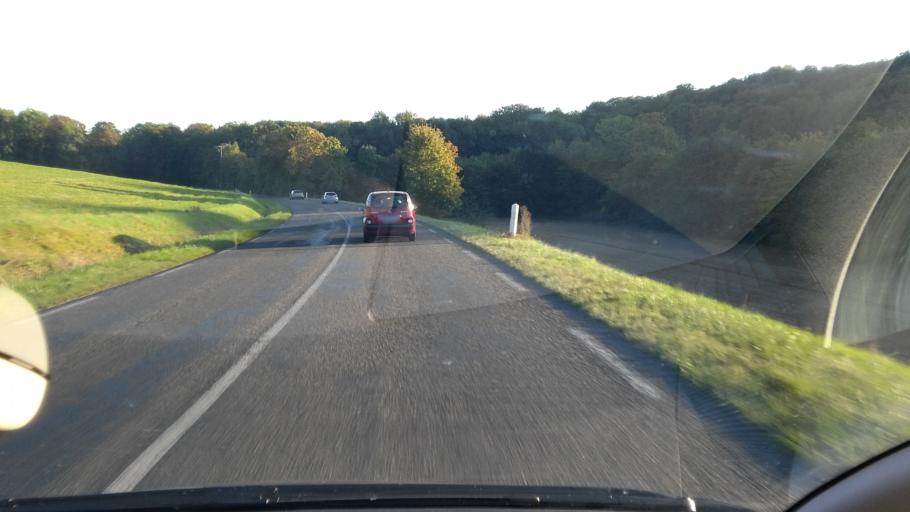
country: FR
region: Champagne-Ardenne
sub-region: Departement de la Marne
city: Verzenay
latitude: 49.1156
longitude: 4.1087
